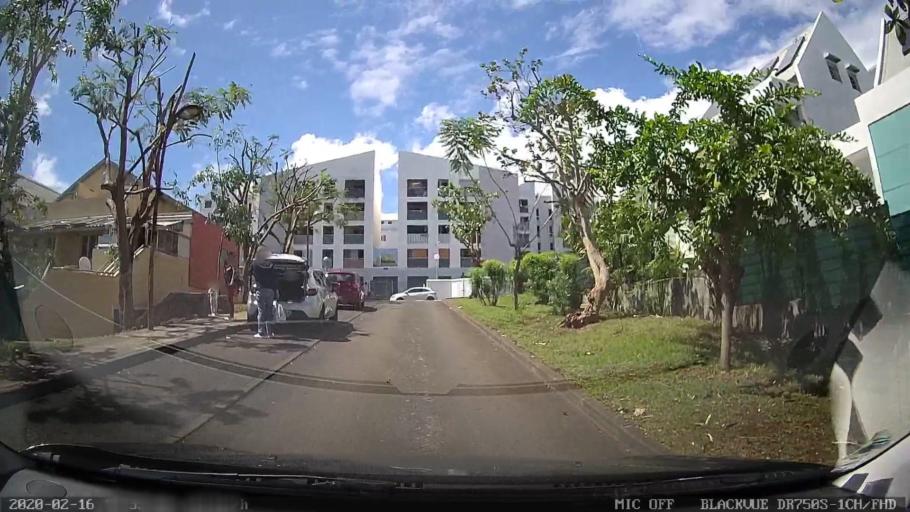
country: RE
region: Reunion
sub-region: Reunion
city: Saint-Denis
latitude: -20.8807
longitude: 55.4411
